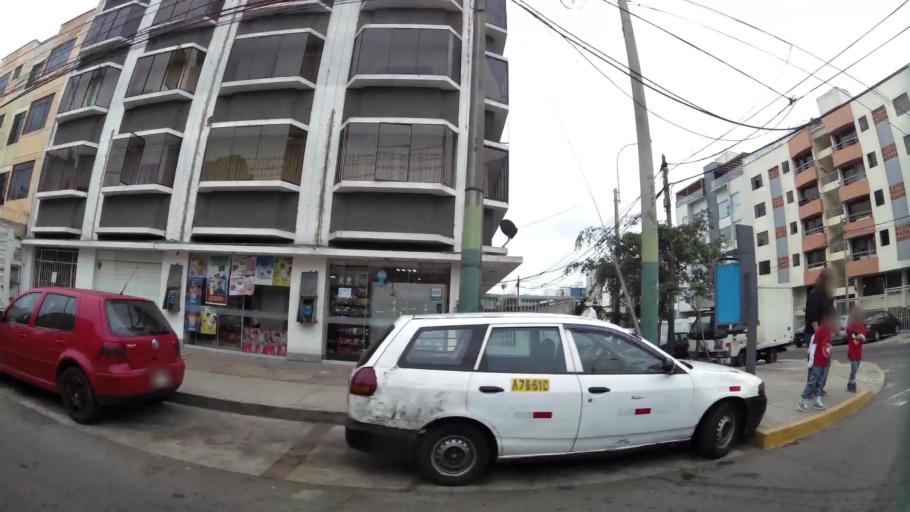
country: PE
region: Lima
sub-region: Lima
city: Surco
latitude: -12.1071
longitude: -77.0088
